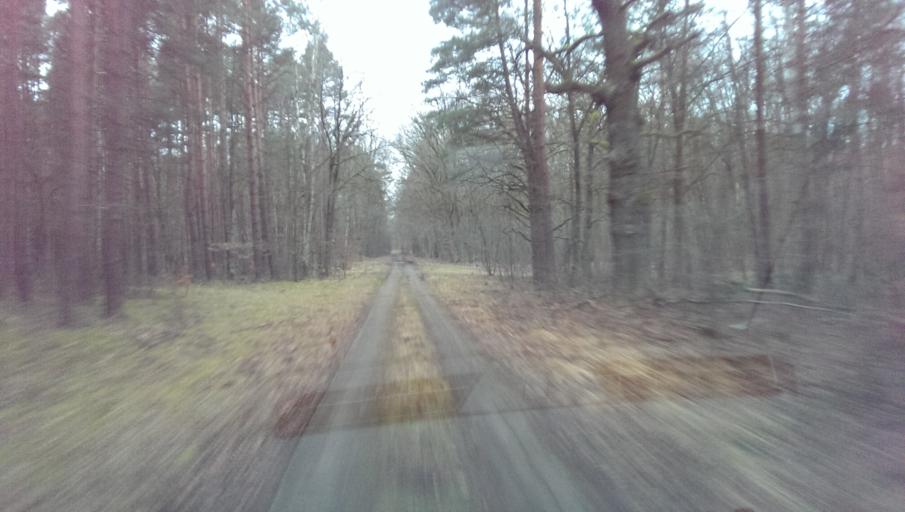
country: DE
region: Brandenburg
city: Sperenberg
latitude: 52.1533
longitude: 13.3278
